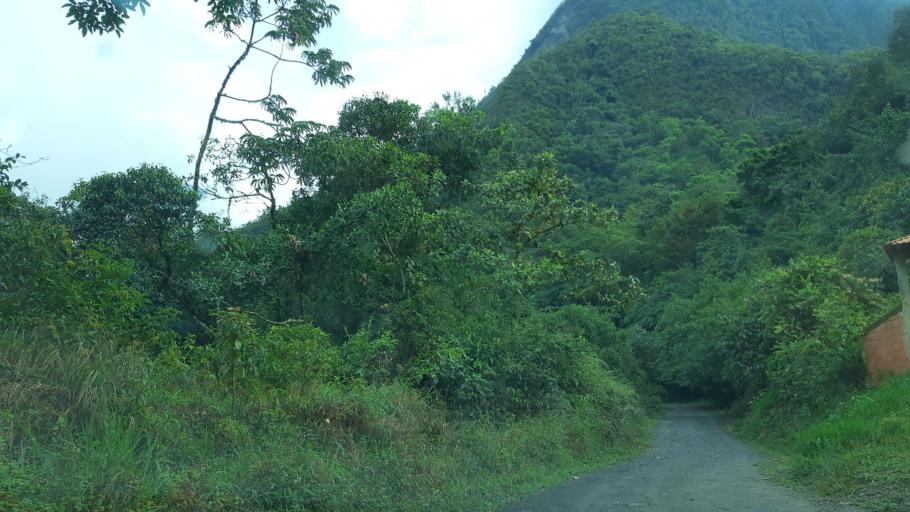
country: CO
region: Boyaca
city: Santa Maria
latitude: 4.9118
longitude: -73.3060
